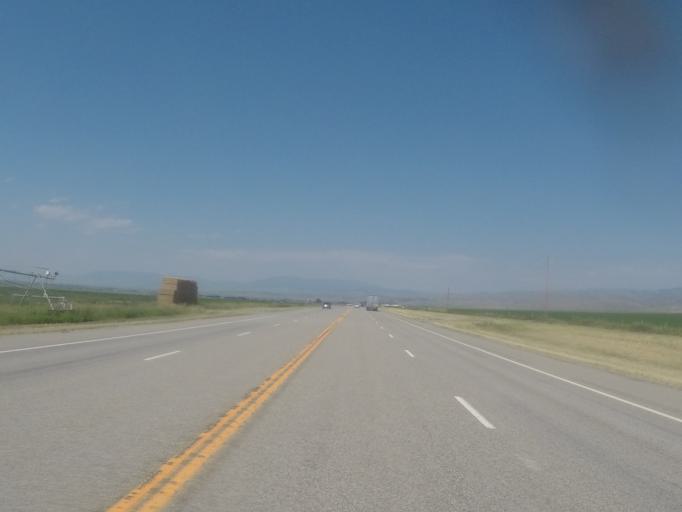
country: US
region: Montana
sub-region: Broadwater County
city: Townsend
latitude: 46.1124
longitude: -111.5057
